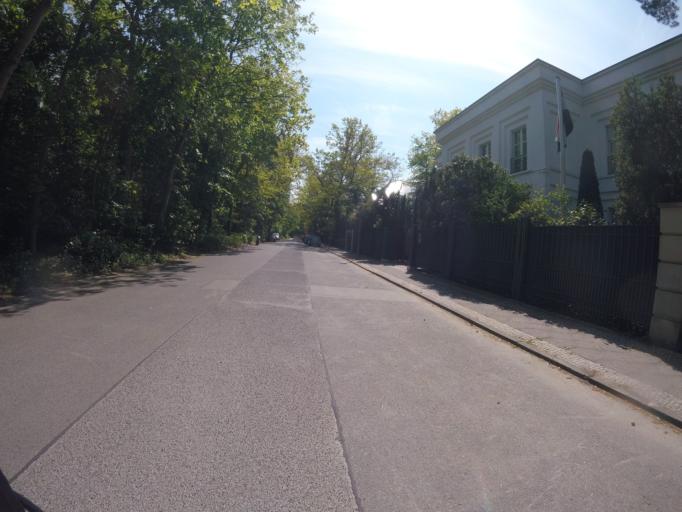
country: DE
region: Berlin
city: Dahlem
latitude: 52.4680
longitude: 13.2767
